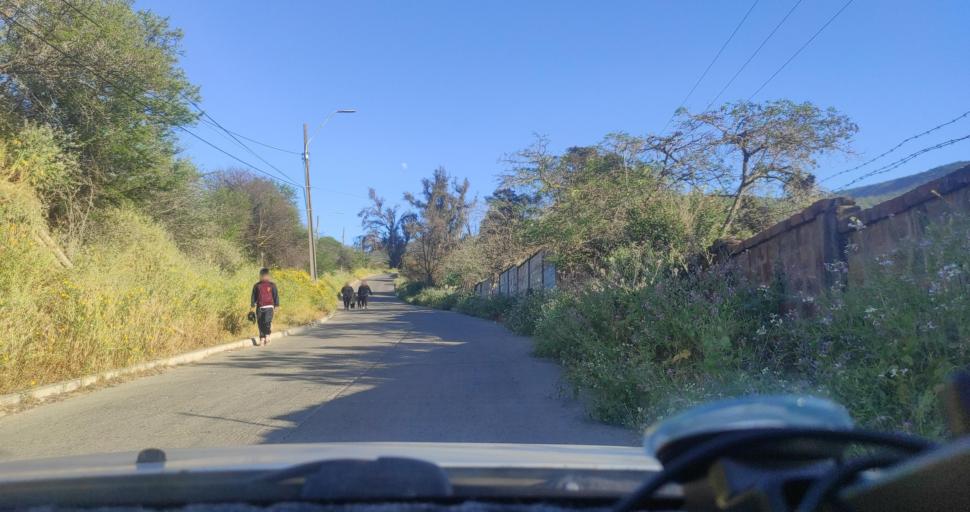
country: CL
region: Valparaiso
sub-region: Provincia de Marga Marga
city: Limache
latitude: -32.9934
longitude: -71.2341
